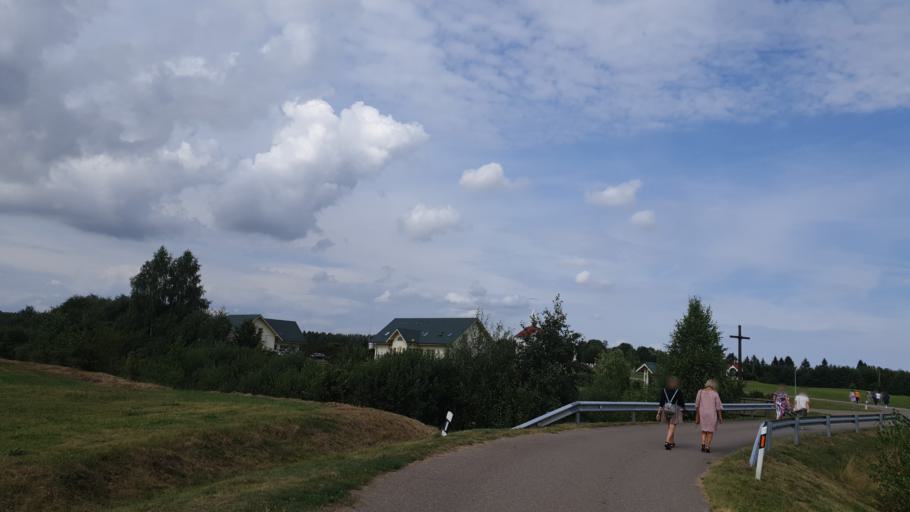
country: LT
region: Vilnius County
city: Elektrenai
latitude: 54.8385
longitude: 24.5657
